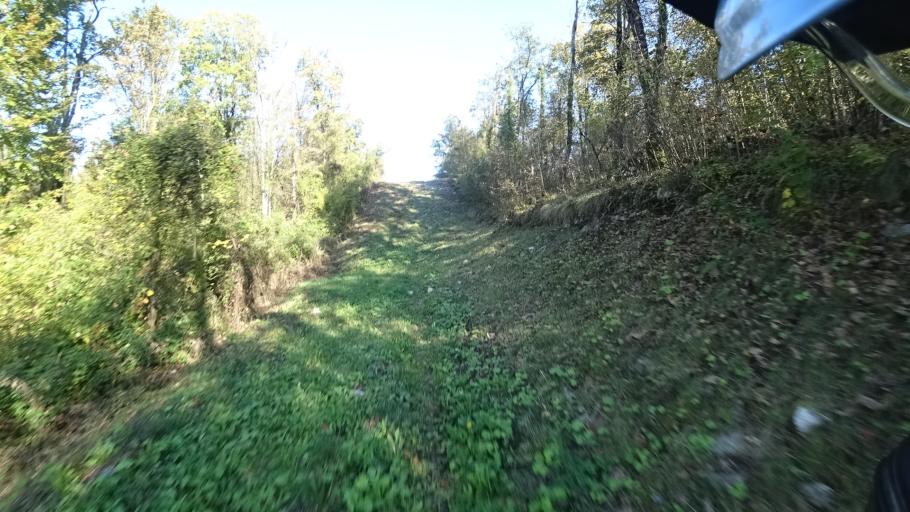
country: HR
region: Primorsko-Goranska
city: Matulji
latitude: 45.3856
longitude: 14.3096
